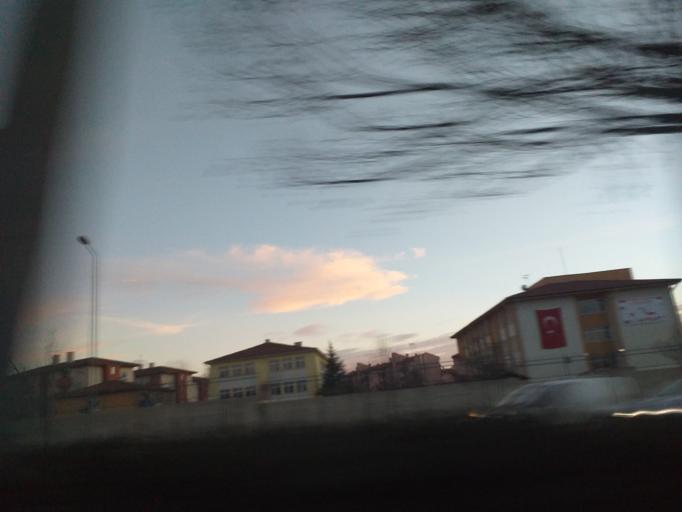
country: TR
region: Ankara
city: Batikent
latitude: 39.9453
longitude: 32.7228
